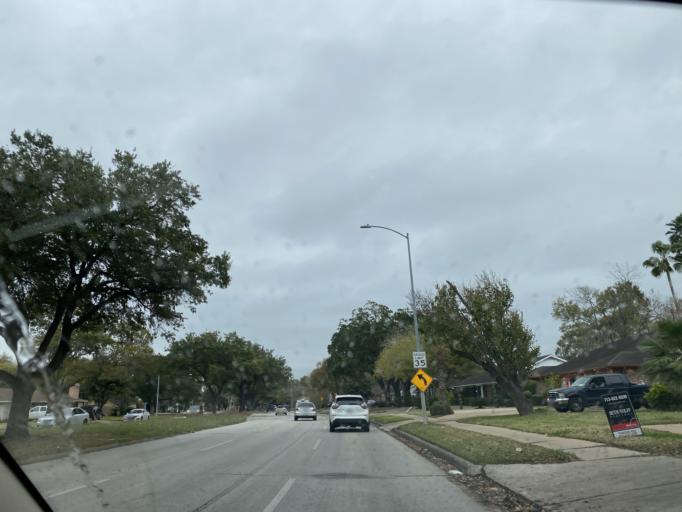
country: US
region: Texas
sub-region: Harris County
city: Piney Point Village
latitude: 29.7292
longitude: -95.5096
